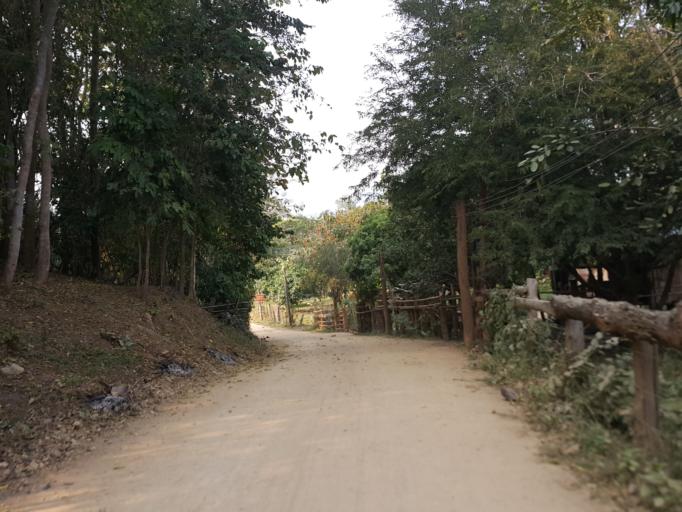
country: TH
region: Lamphun
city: Li
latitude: 17.6067
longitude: 98.9638
